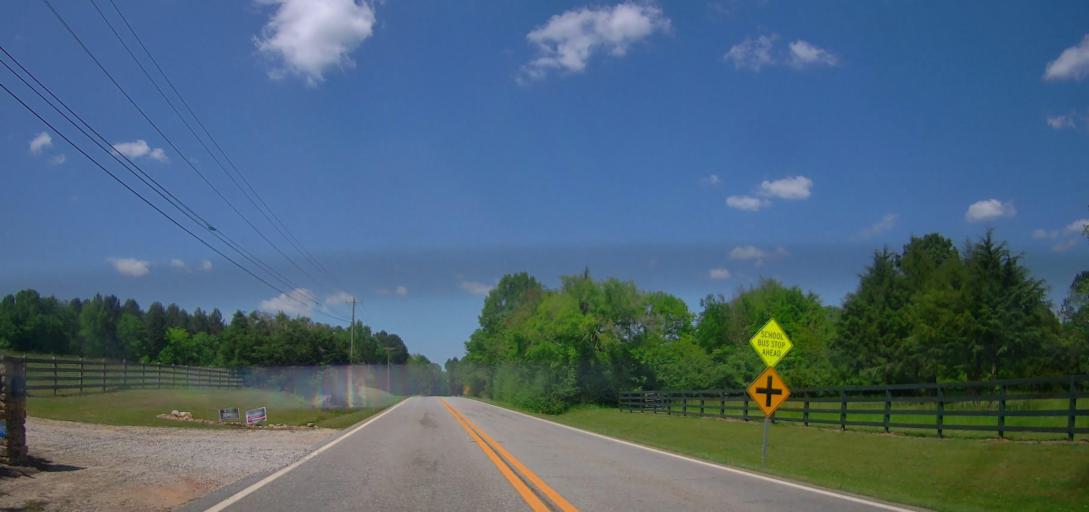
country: US
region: Georgia
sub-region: Putnam County
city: Eatonton
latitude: 33.3018
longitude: -83.3034
